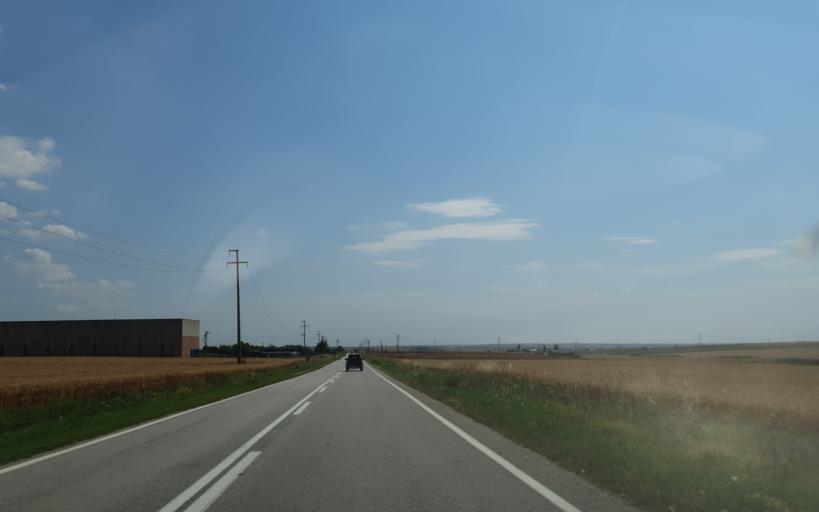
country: TR
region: Kirklareli
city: Buyukkaristiran
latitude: 41.3204
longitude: 27.5235
